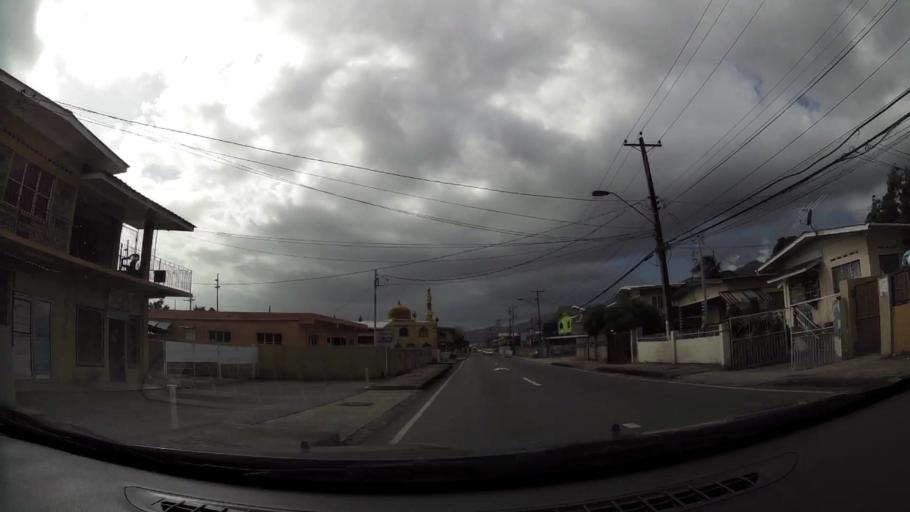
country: TT
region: Tunapuna/Piarco
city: Paradise
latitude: 10.6419
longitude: -61.3558
